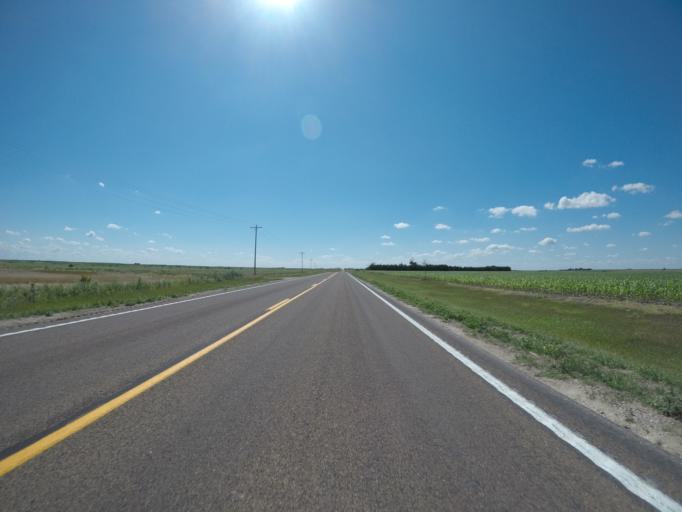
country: US
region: Nebraska
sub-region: Chase County
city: Imperial
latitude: 40.5376
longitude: -101.7554
